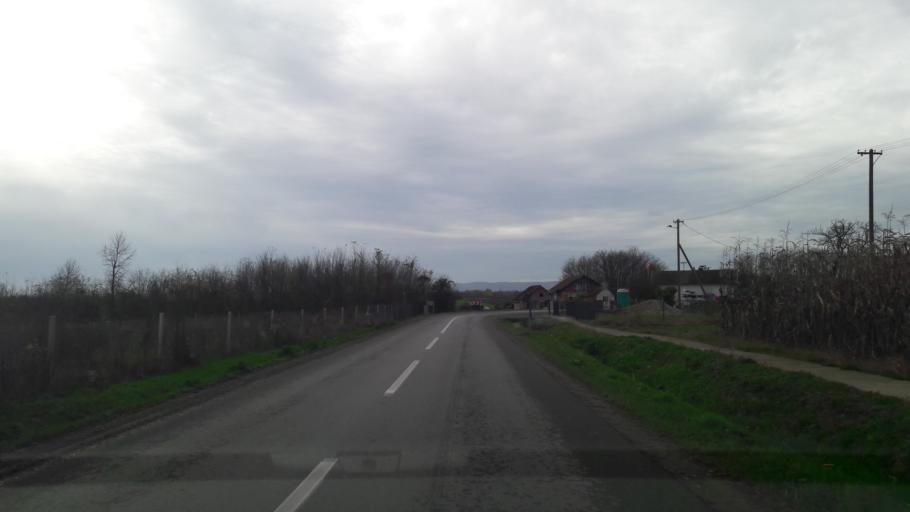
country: HR
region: Osjecko-Baranjska
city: Fericanci
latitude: 45.5245
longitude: 18.0136
